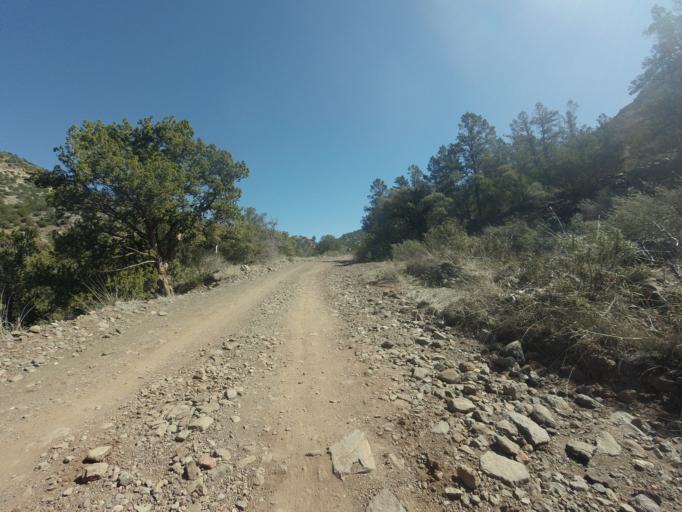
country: US
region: Arizona
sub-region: Gila County
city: Pine
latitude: 34.4047
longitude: -111.6157
